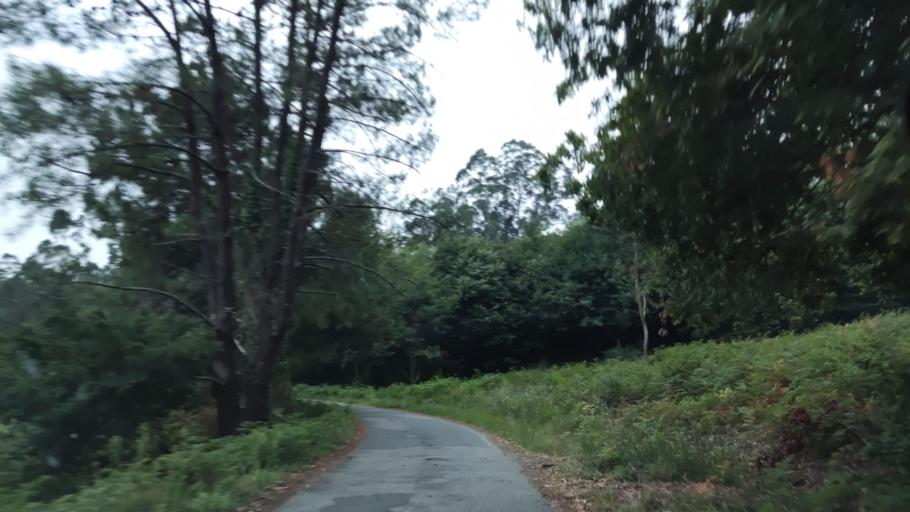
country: ES
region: Galicia
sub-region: Provincia de Pontevedra
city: Catoira
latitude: 42.6930
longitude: -8.7326
